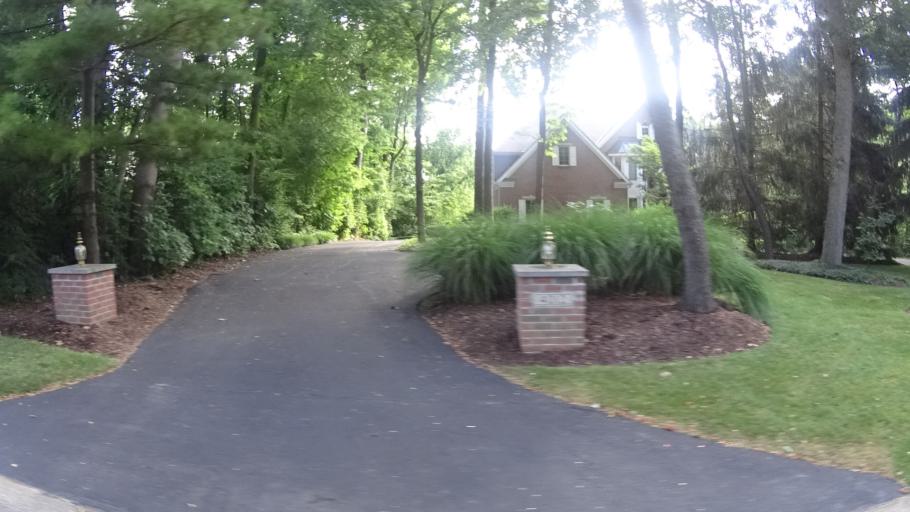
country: US
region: Ohio
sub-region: Erie County
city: Sandusky
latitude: 41.4177
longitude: -82.6599
